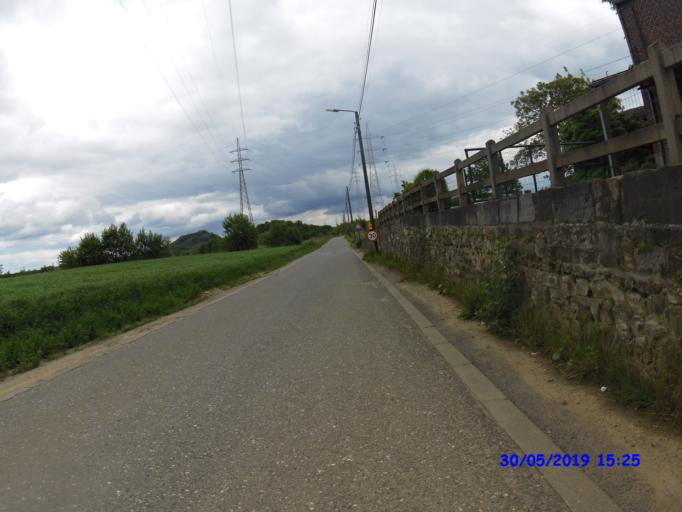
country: BE
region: Wallonia
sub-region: Province du Hainaut
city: Courcelles
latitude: 50.3940
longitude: 4.3491
